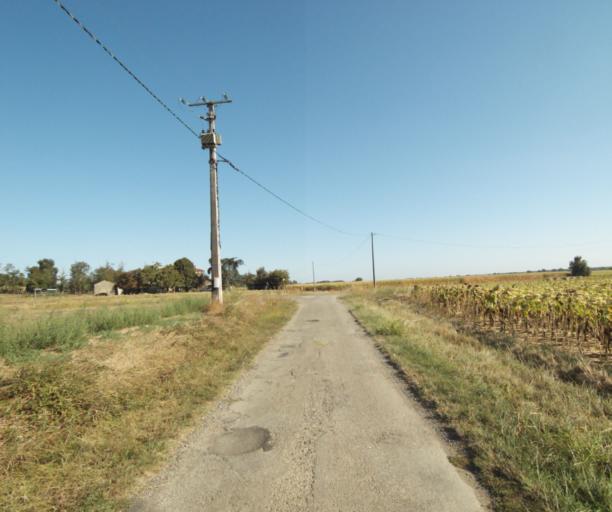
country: FR
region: Midi-Pyrenees
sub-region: Departement du Tarn-et-Garonne
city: Verdun-sur-Garonne
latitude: 43.8625
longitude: 1.1961
